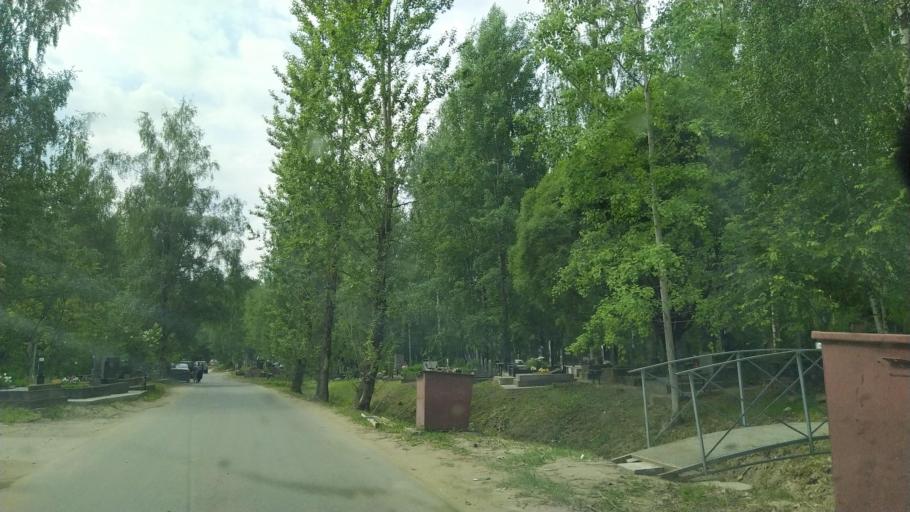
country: RU
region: St.-Petersburg
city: Dachnoye
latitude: 59.7659
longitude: 30.2620
